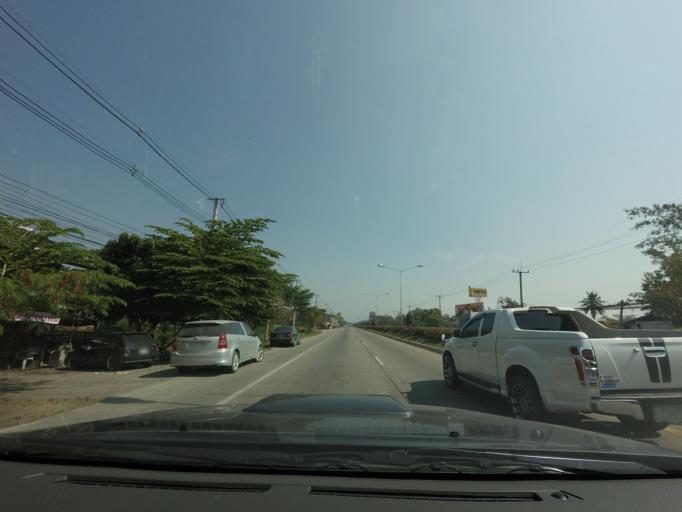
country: TH
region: Chiang Mai
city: San Sai
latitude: 18.8208
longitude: 99.0408
